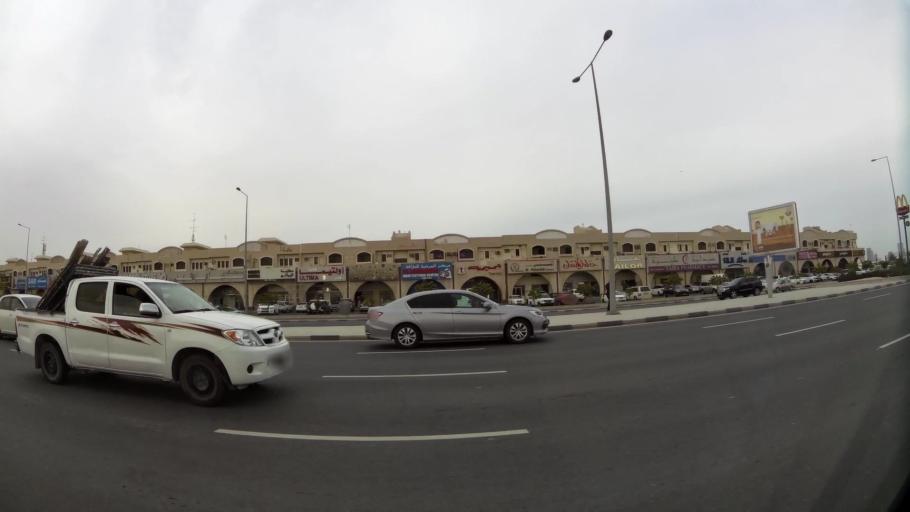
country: QA
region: Baladiyat ad Dawhah
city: Doha
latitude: 25.3210
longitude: 51.4885
